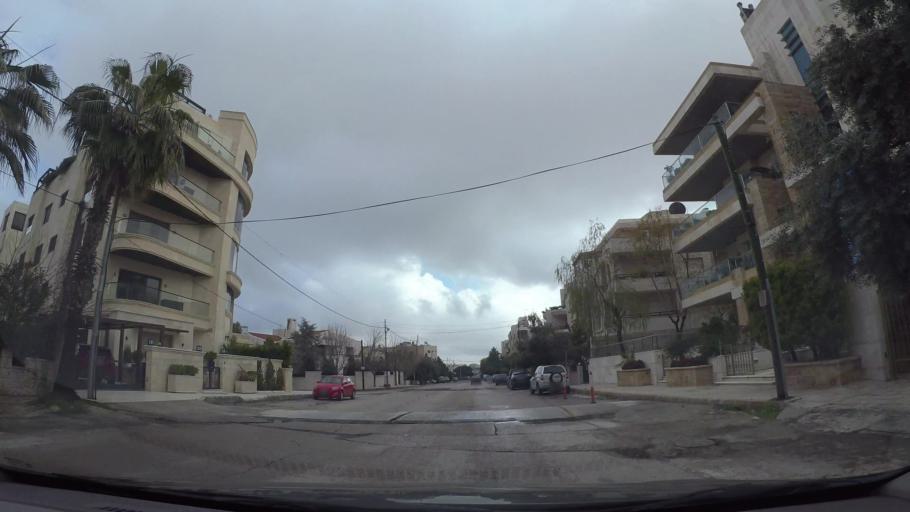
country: JO
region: Amman
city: Wadi as Sir
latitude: 31.9489
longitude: 35.8760
